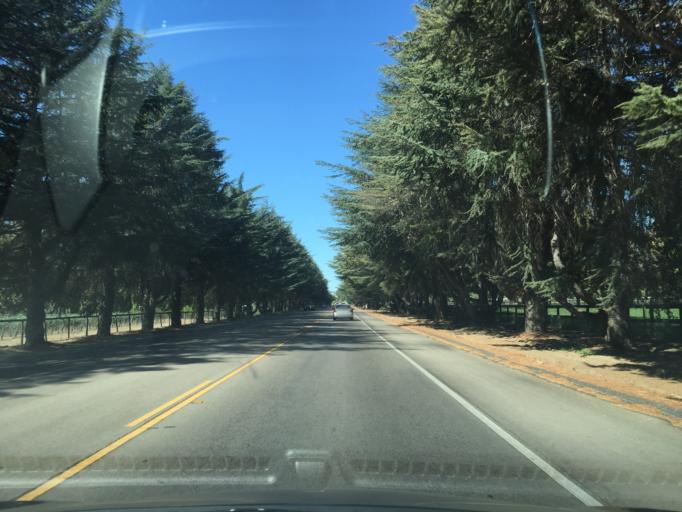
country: US
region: California
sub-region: Santa Barbara County
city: Buellton
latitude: 34.6035
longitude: -120.1693
